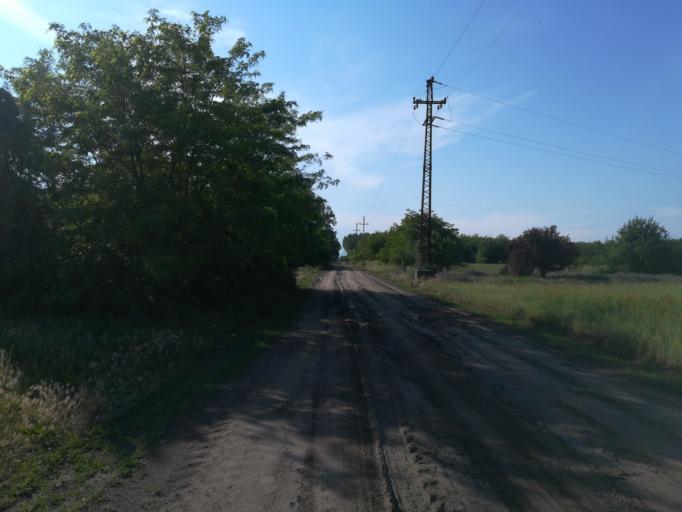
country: HU
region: Bacs-Kiskun
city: Tiszakecske
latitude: 46.9437
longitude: 20.0860
